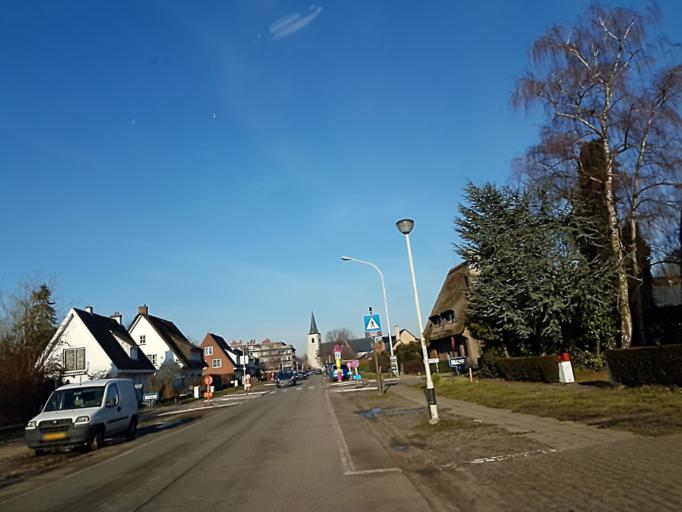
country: BE
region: Flanders
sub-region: Provincie Antwerpen
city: Hove
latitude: 51.1515
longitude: 4.4718
